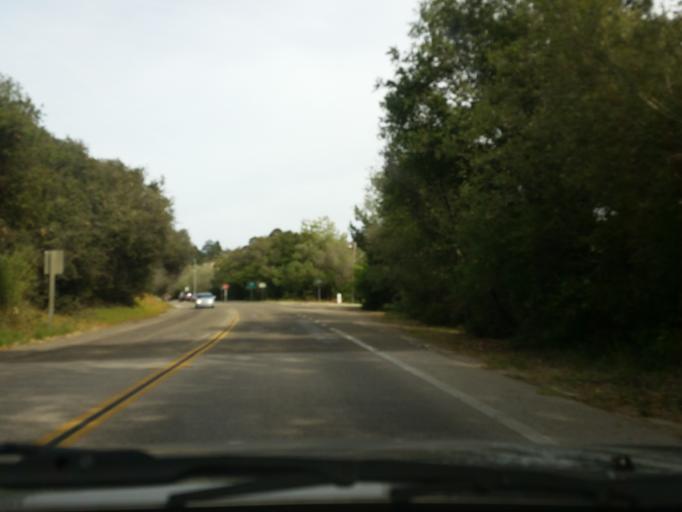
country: US
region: California
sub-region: San Luis Obispo County
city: Grover Beach
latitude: 35.1313
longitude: -120.6130
